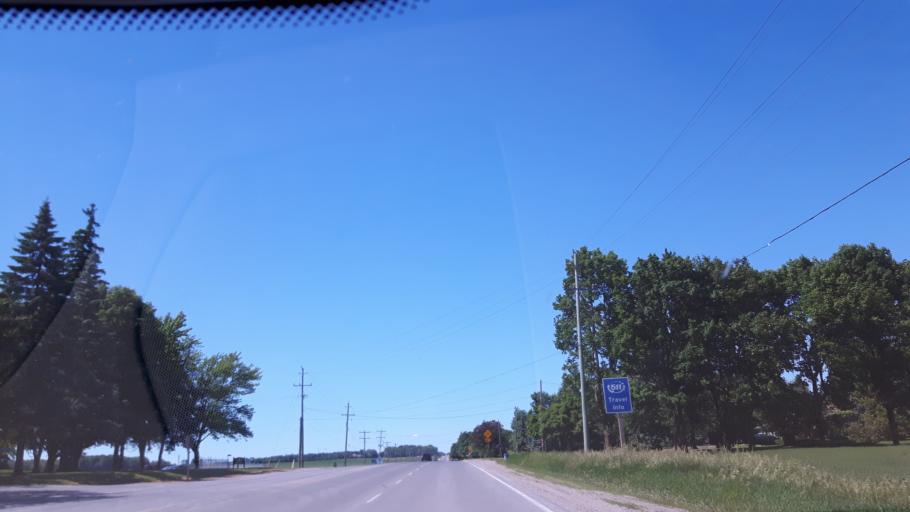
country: CA
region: Ontario
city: London
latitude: 43.0570
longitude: -81.2983
